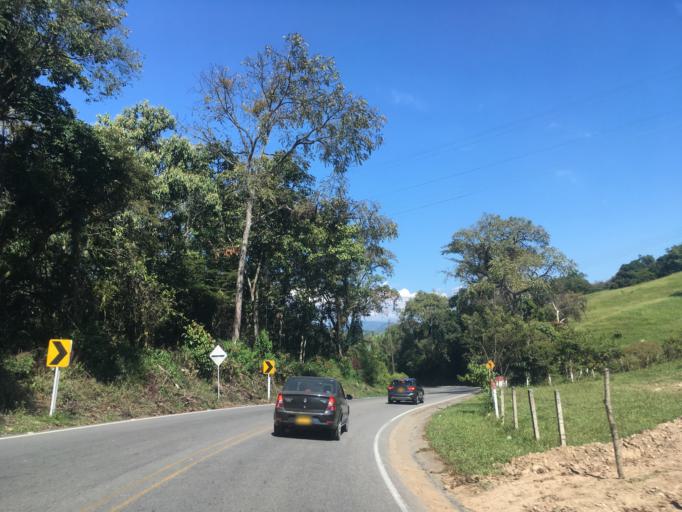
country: CO
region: Santander
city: Suaita
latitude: 6.0632
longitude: -73.4298
